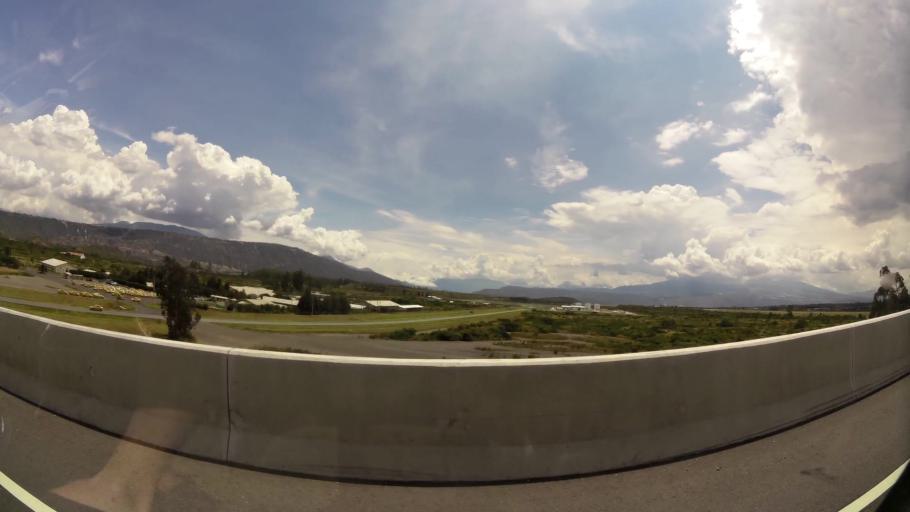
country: EC
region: Pichincha
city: Quito
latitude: -0.1238
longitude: -78.3612
